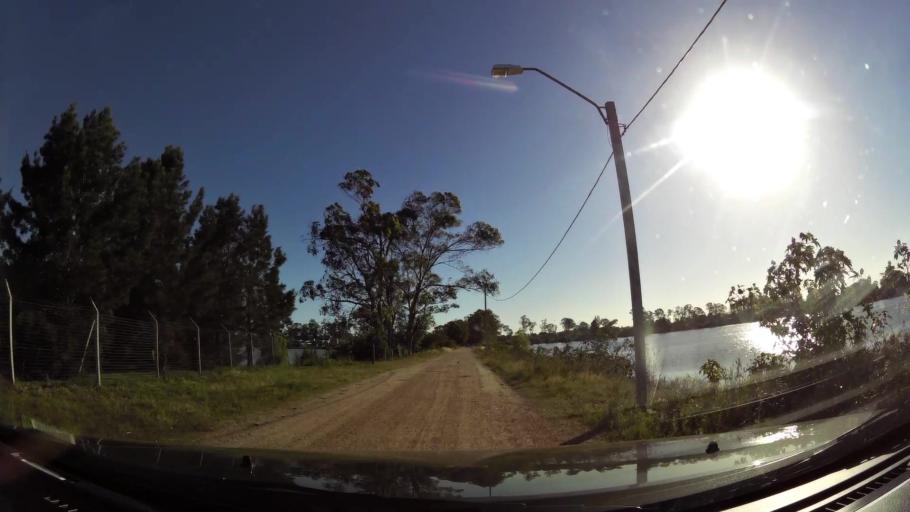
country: UY
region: Canelones
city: Paso de Carrasco
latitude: -34.8612
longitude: -56.0411
